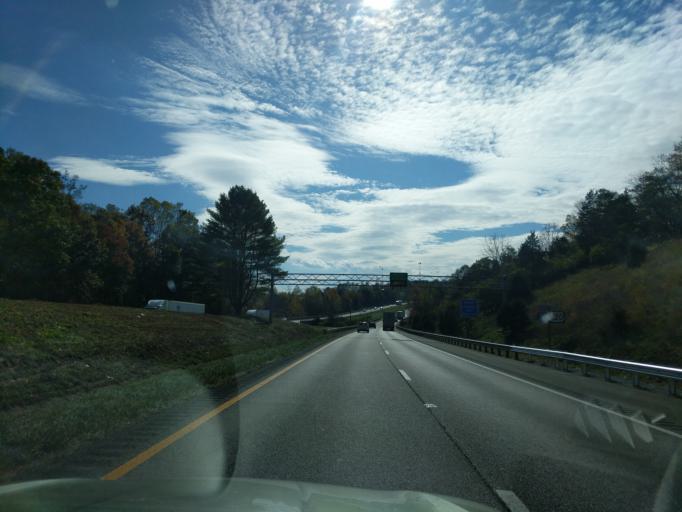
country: US
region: Virginia
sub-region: Botetourt County
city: Cloverdale
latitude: 37.3806
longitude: -79.9083
